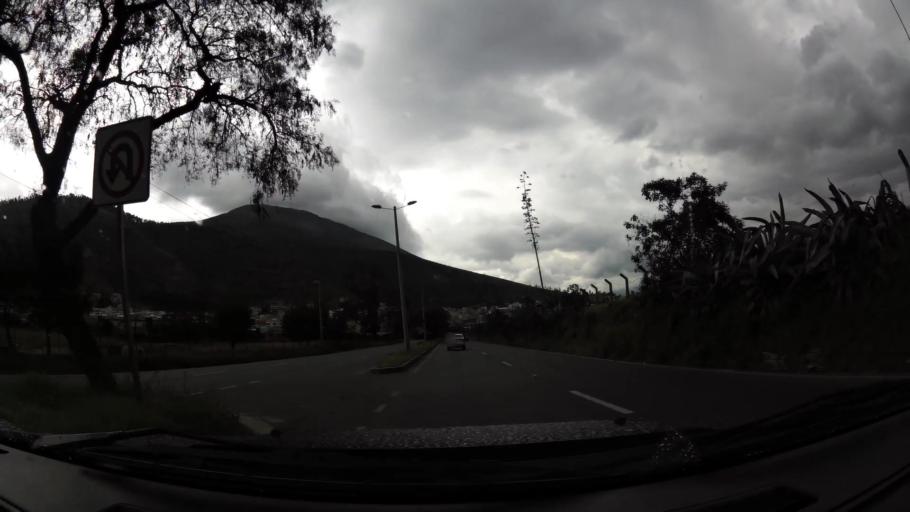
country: EC
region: Pichincha
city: Quito
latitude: -0.0775
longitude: -78.4809
